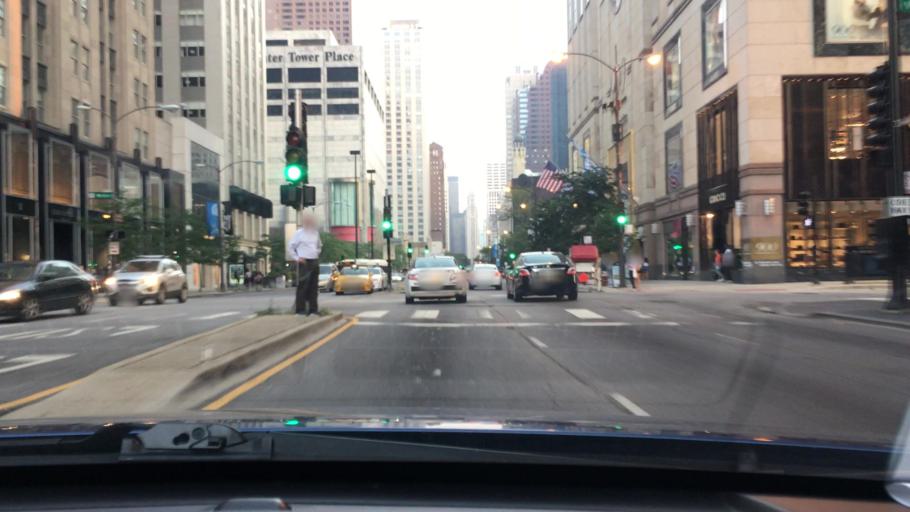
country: US
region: Illinois
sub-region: Cook County
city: Chicago
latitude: 41.9002
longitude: -87.6242
